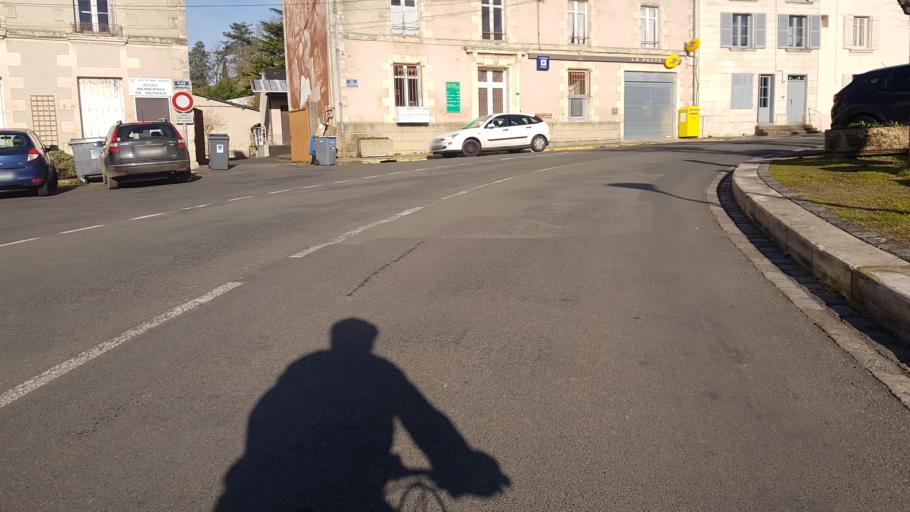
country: FR
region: Poitou-Charentes
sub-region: Departement de la Vienne
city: Migne-Auxances
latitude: 46.6268
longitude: 0.3110
